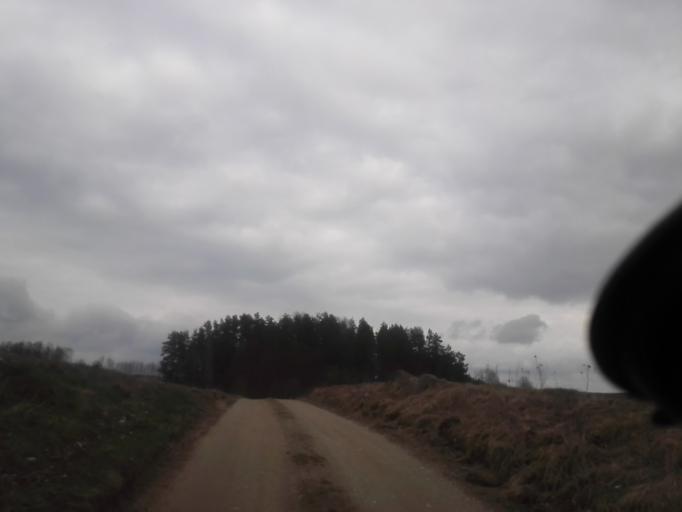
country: PL
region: Podlasie
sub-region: Suwalki
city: Suwalki
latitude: 54.2527
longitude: 22.9220
